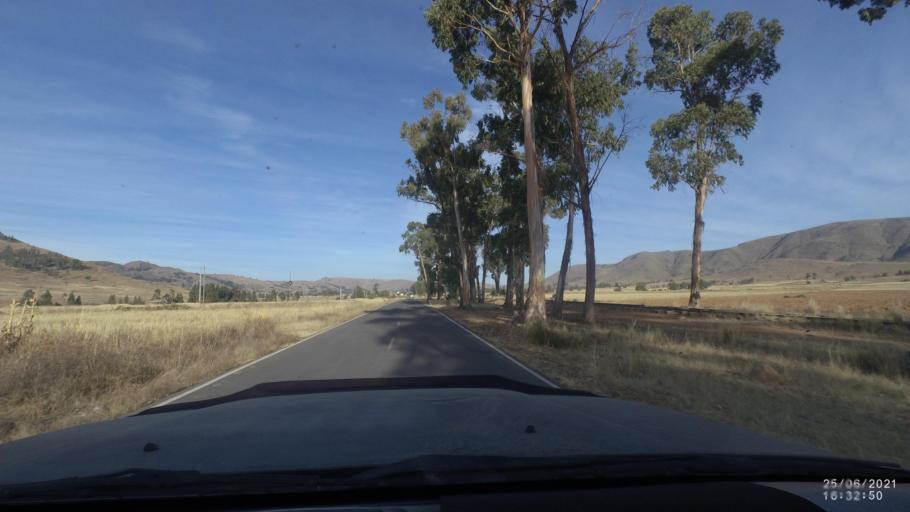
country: BO
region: Cochabamba
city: Arani
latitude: -17.8096
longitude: -65.7911
